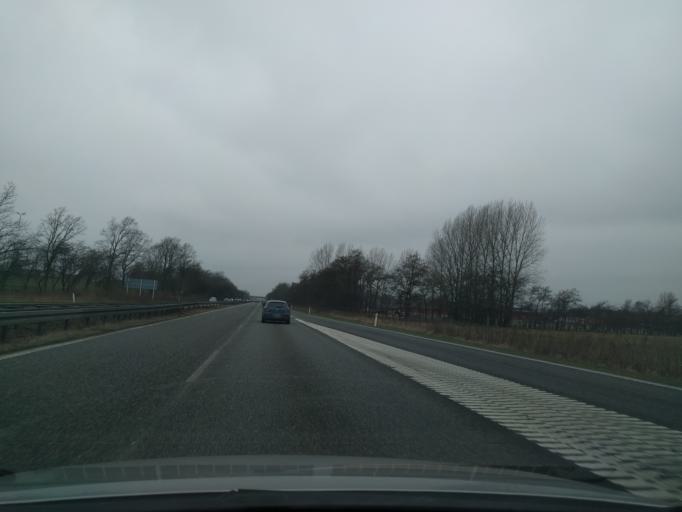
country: DK
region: Zealand
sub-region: Slagelse Kommune
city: Forlev
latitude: 55.3800
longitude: 11.3057
